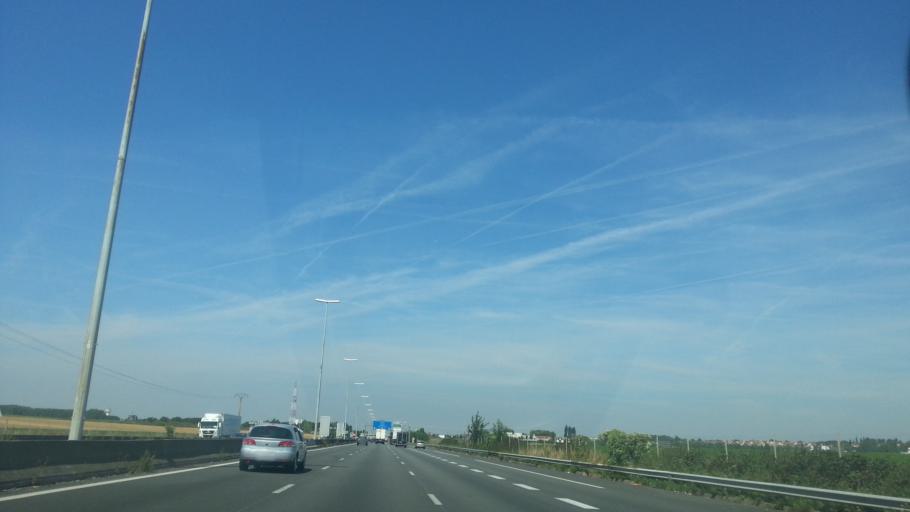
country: FR
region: Ile-de-France
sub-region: Departement du Val-d'Oise
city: Vemars
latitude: 49.0780
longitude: 2.5518
